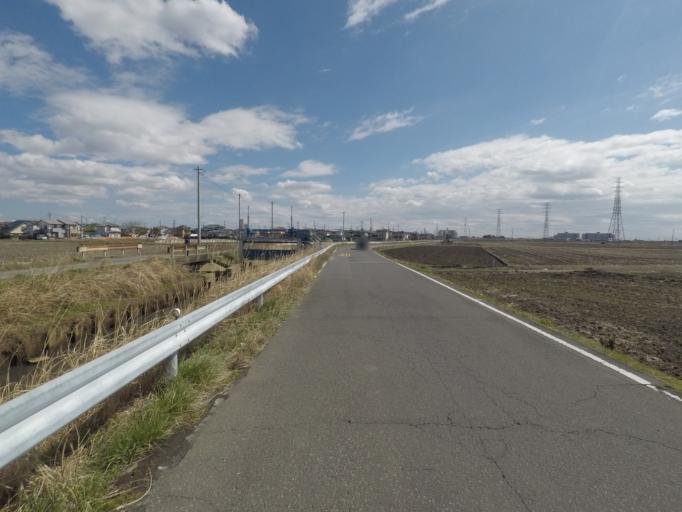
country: JP
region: Ibaraki
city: Fujishiro
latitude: 35.9373
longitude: 140.1163
